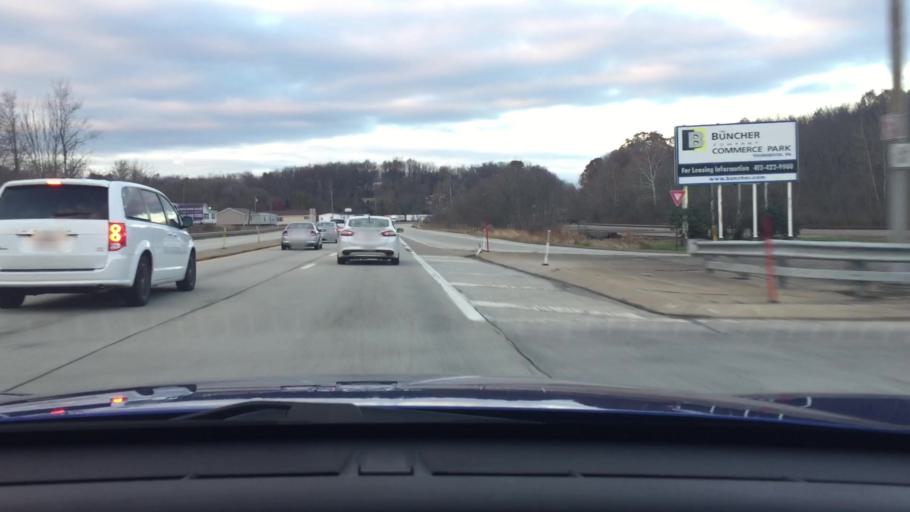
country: US
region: Pennsylvania
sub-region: Westmoreland County
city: Youngwood
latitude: 40.2541
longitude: -79.5710
